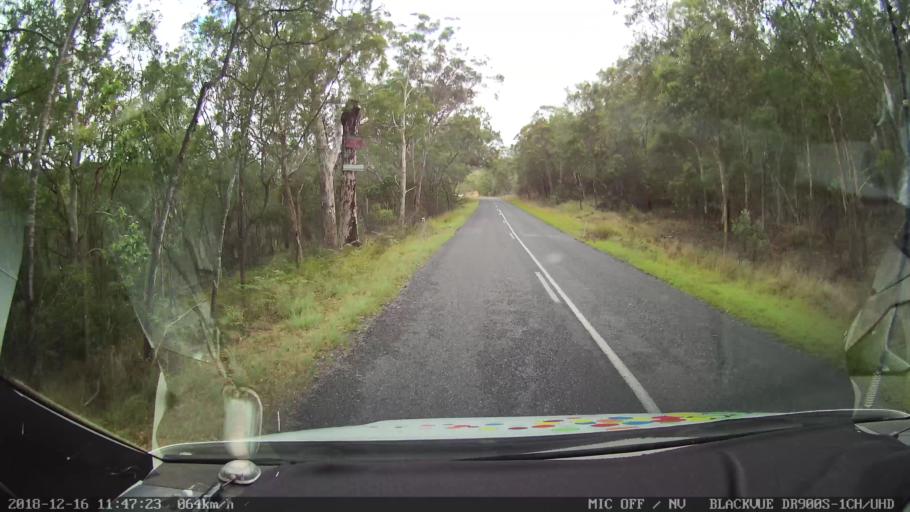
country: AU
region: New South Wales
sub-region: Tenterfield Municipality
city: Carrolls Creek
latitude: -28.9215
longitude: 152.2374
